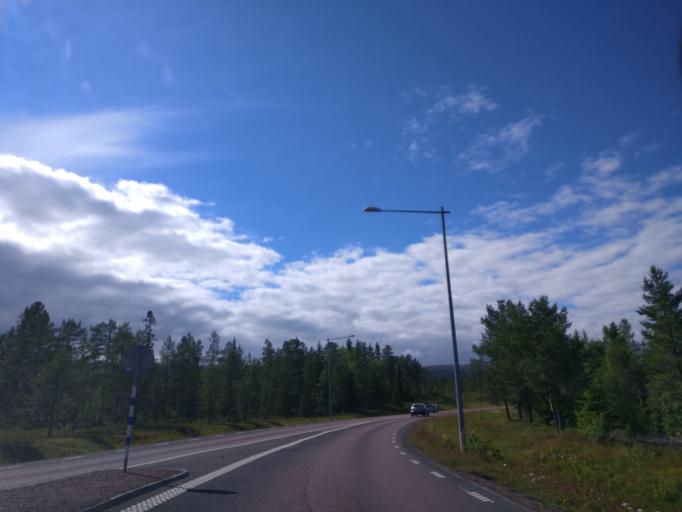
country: SE
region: Dalarna
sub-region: Malung-Saelens kommun
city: Malung
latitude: 61.1656
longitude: 13.1984
